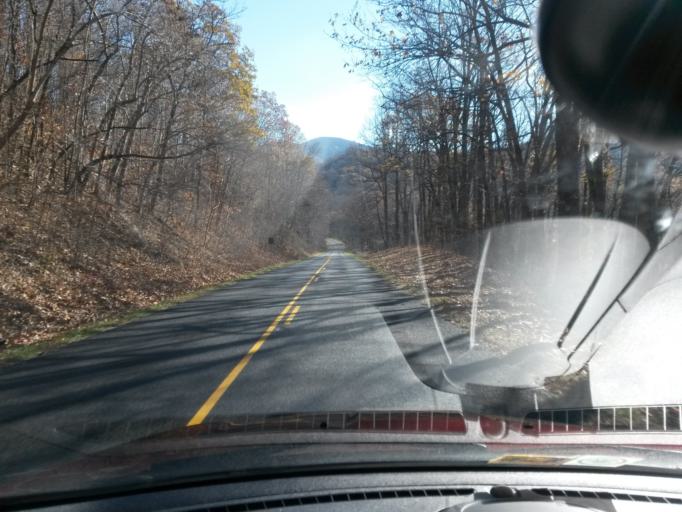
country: US
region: Virginia
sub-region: Botetourt County
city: Buchanan
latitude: 37.4741
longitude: -79.6458
